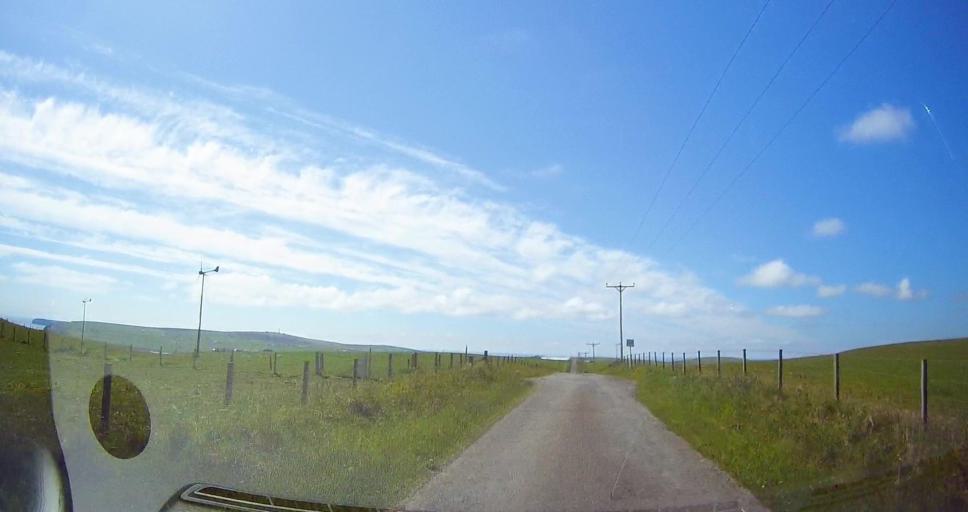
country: GB
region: Scotland
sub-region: Orkney Islands
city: Kirkwall
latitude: 58.8117
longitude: -2.9264
